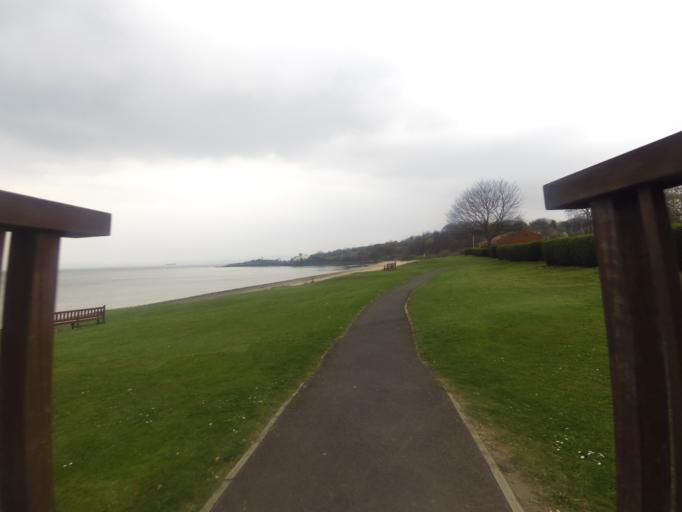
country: GB
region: Scotland
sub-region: Fife
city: Aberdour
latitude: 56.0555
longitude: -3.2854
